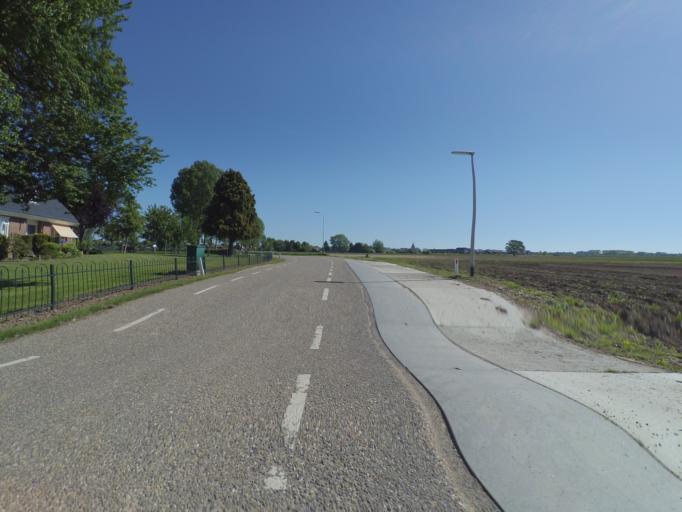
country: NL
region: Gelderland
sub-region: Gemeente Zutphen
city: Zutphen
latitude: 52.1345
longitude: 6.1742
